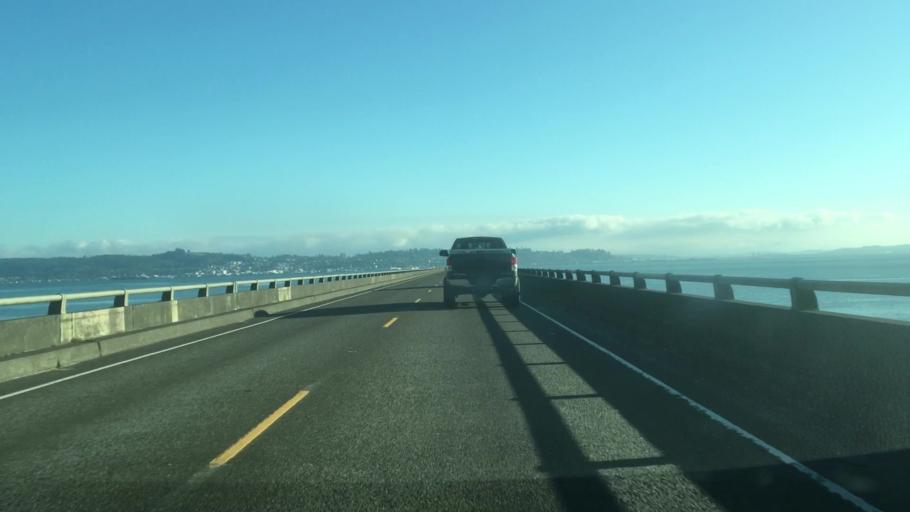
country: US
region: Oregon
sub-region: Clatsop County
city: Astoria
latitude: 46.2319
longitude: -123.8704
